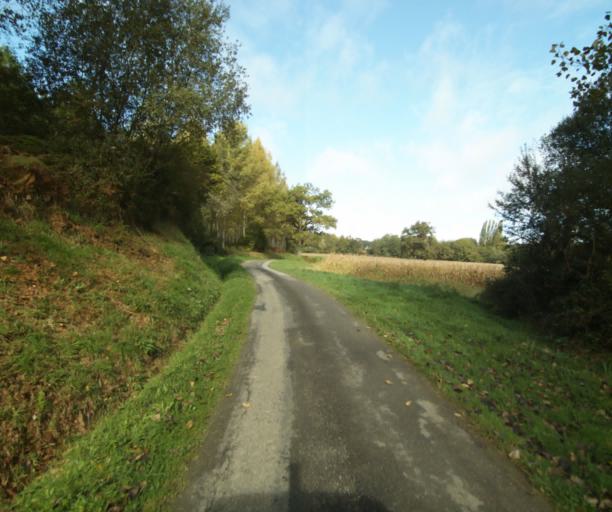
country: FR
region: Midi-Pyrenees
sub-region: Departement du Gers
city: Cazaubon
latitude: 43.8615
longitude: -0.0997
